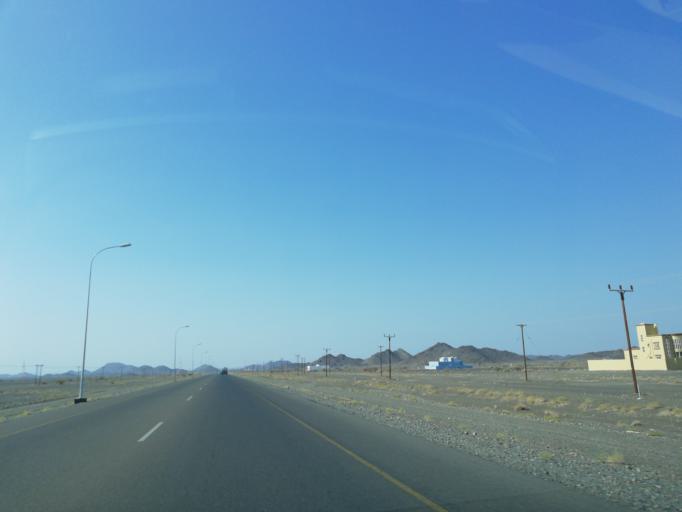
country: OM
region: Ash Sharqiyah
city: Ibra'
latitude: 22.7616
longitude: 58.1458
